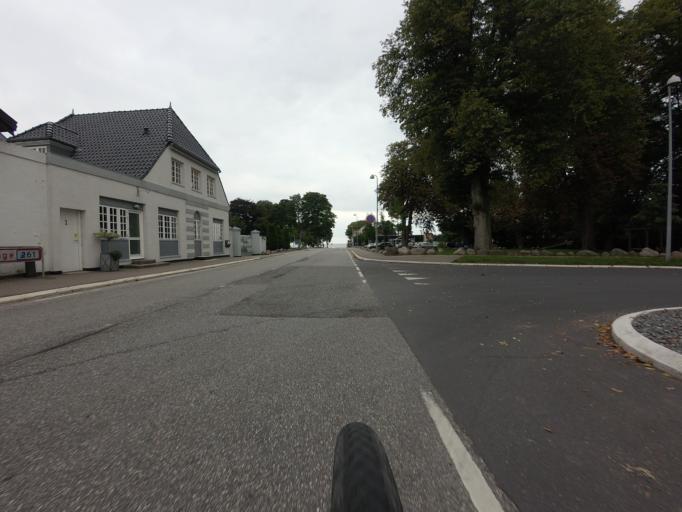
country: DK
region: Zealand
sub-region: Stevns Kommune
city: Store Heddinge
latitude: 55.2555
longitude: 12.3798
